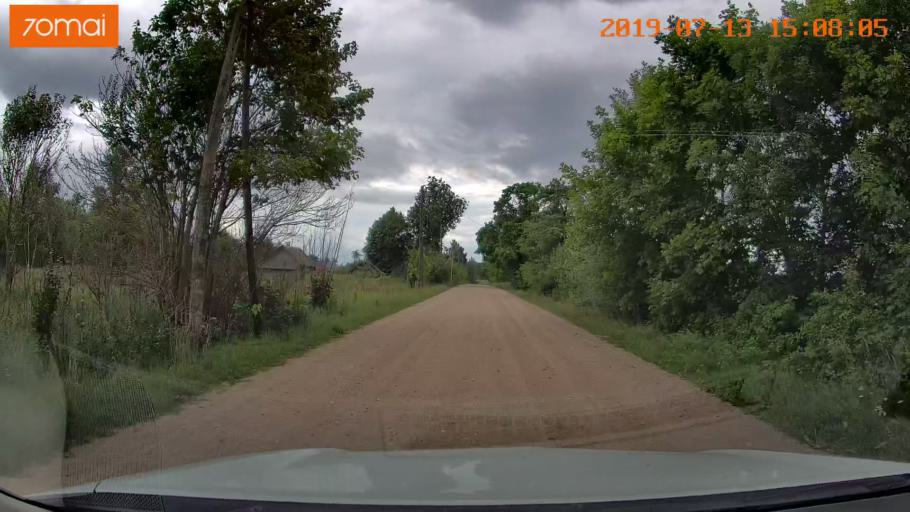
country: BY
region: Mogilev
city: Hlusha
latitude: 53.1826
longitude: 28.7573
